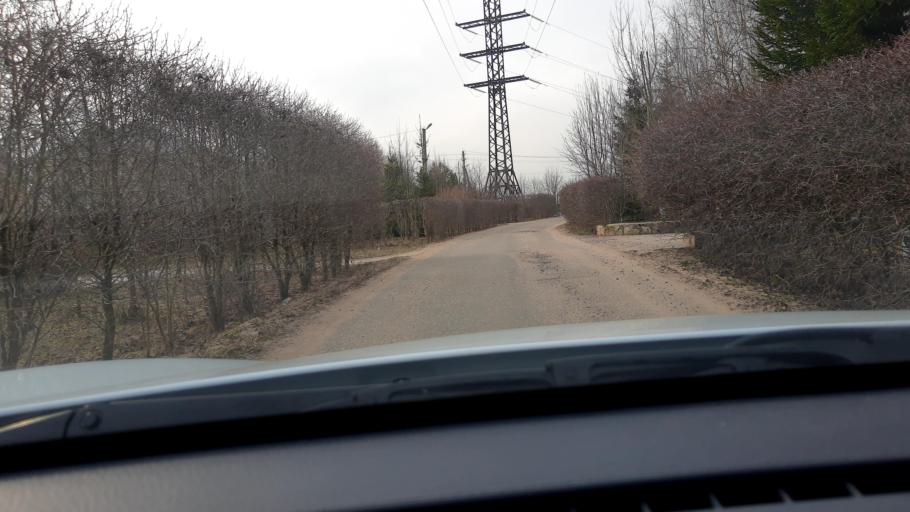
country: RU
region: Moskovskaya
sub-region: Leninskiy Rayon
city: Molokovo
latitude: 55.4910
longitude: 37.8532
